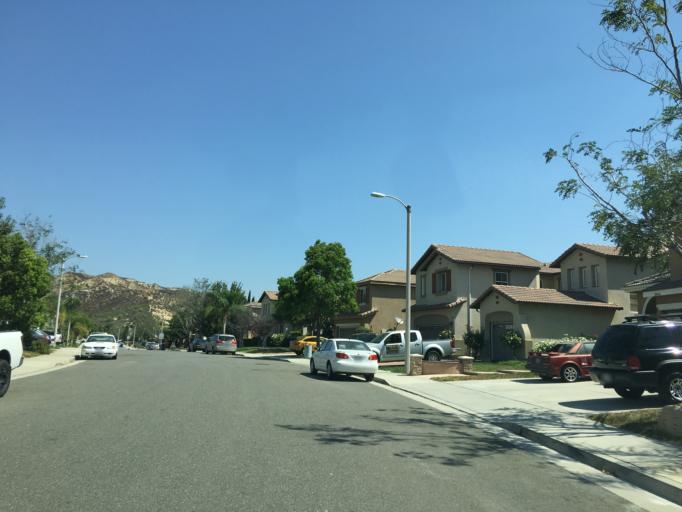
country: US
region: California
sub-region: Los Angeles County
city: Castaic
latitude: 34.4689
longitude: -118.6417
